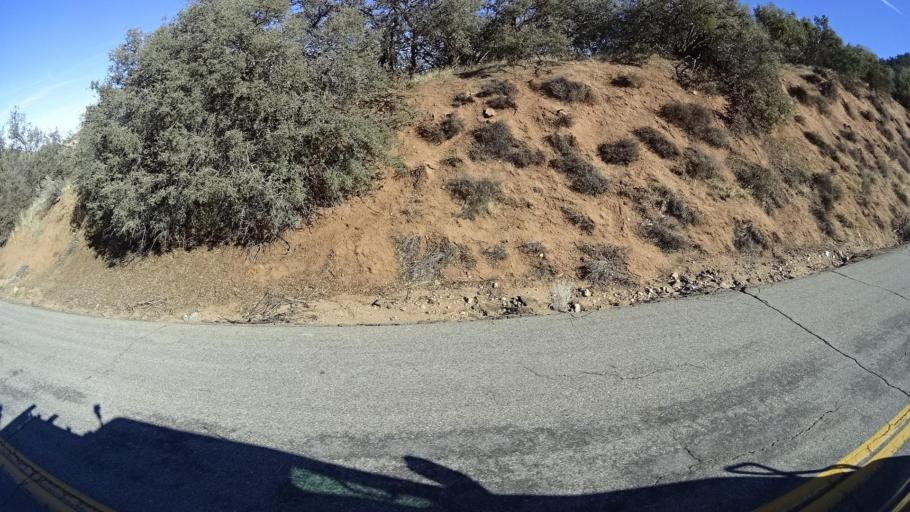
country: US
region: California
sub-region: Kern County
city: Maricopa
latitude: 34.8791
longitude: -119.3562
